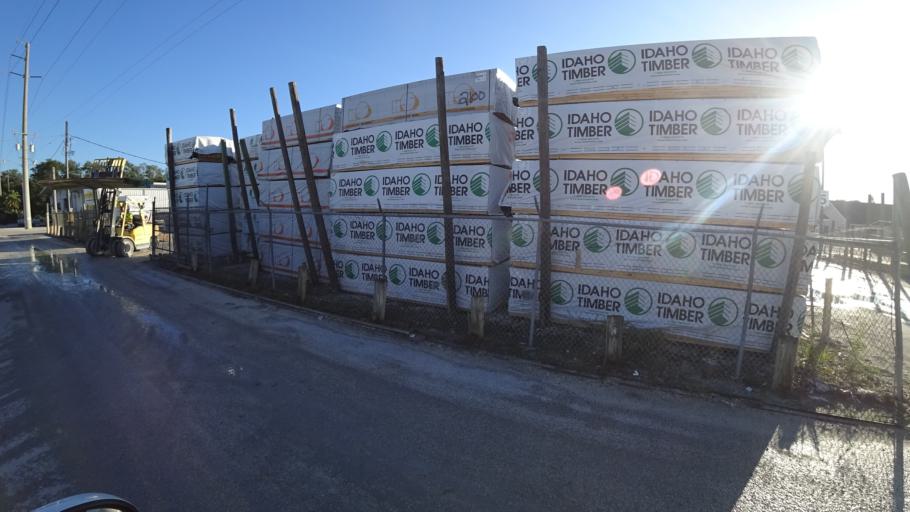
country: US
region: Florida
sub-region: Manatee County
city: Bradenton
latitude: 27.4923
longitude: -82.5578
